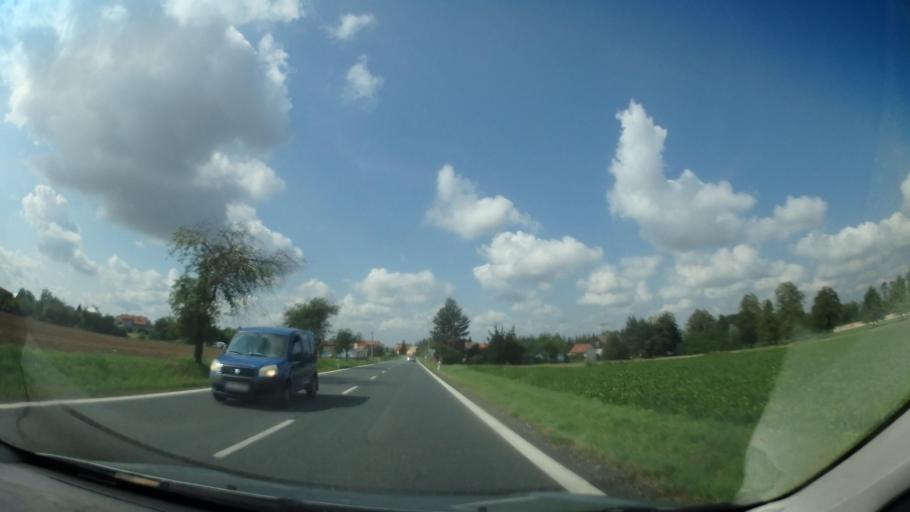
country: CZ
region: Central Bohemia
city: Suchdol
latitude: 49.9525
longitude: 15.1766
